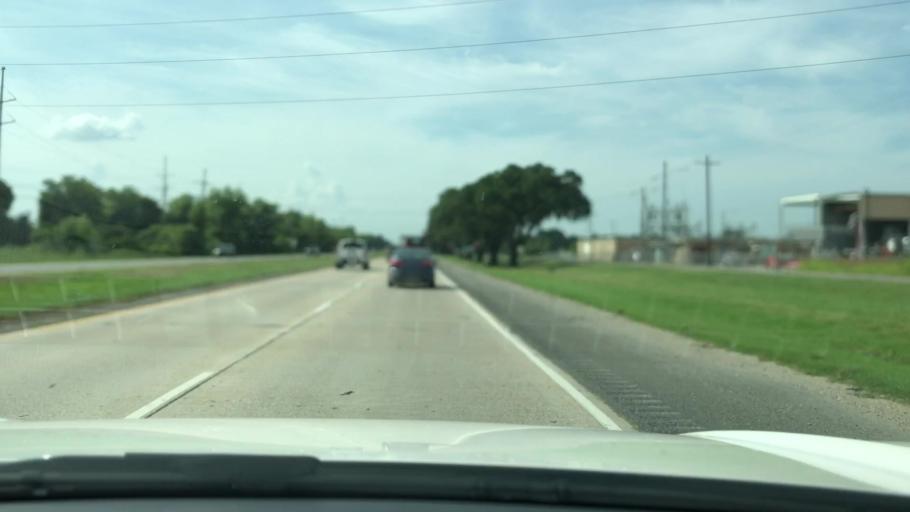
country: US
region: Louisiana
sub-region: West Baton Rouge Parish
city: Addis
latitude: 30.3227
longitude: -91.2526
